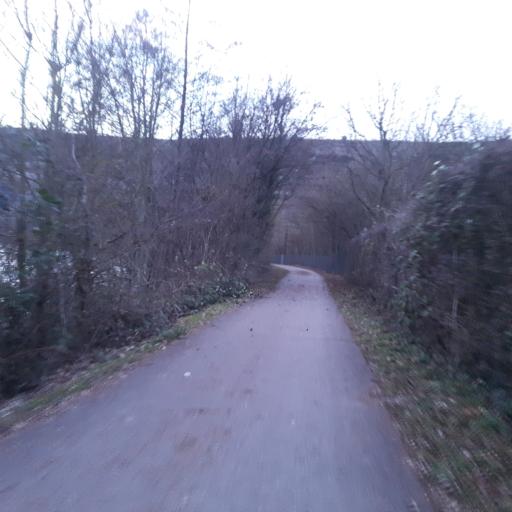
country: DE
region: Baden-Wuerttemberg
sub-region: Regierungsbezirk Stuttgart
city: Mundelsheim
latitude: 49.0017
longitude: 9.2010
